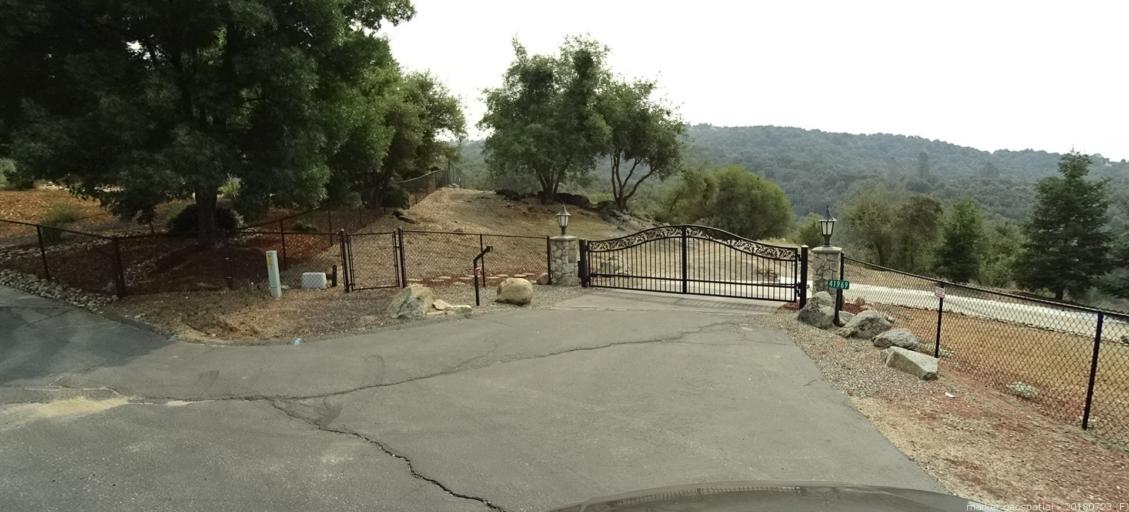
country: US
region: California
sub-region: Madera County
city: Oakhurst
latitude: 37.3595
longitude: -119.6764
